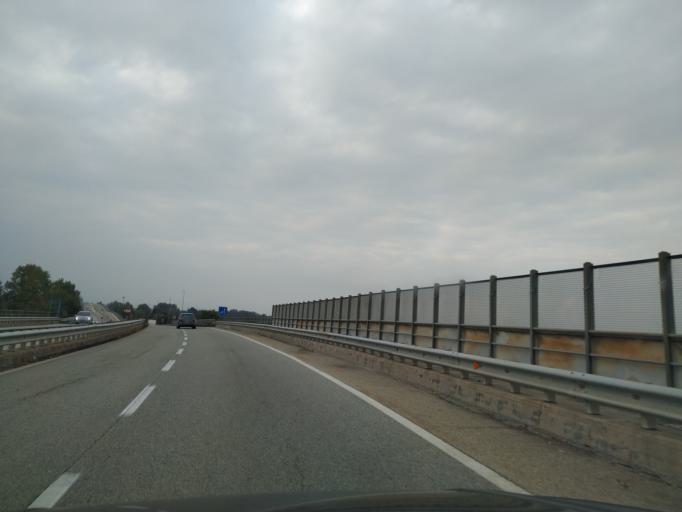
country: IT
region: Piedmont
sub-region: Provincia di Torino
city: Brandizzo
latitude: 45.1872
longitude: 7.8581
